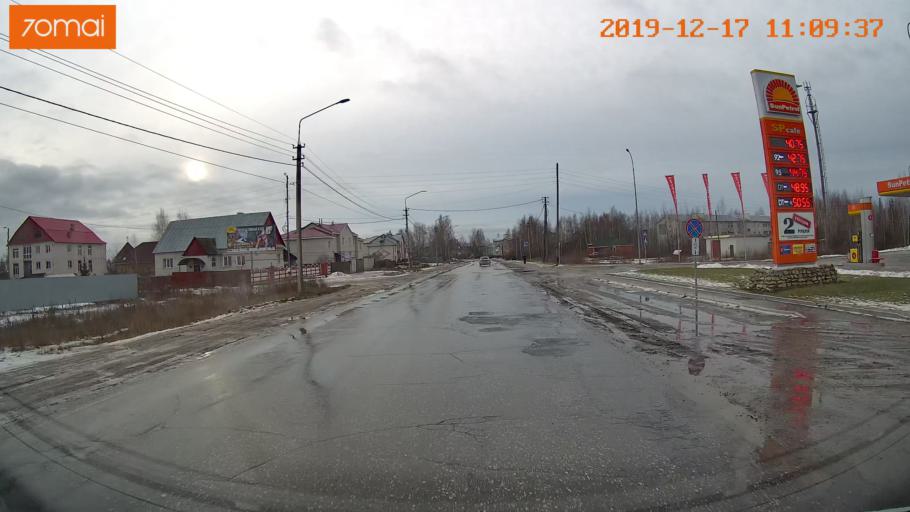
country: RU
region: Vladimir
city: Gus'-Khrustal'nyy
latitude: 55.5991
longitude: 40.6422
